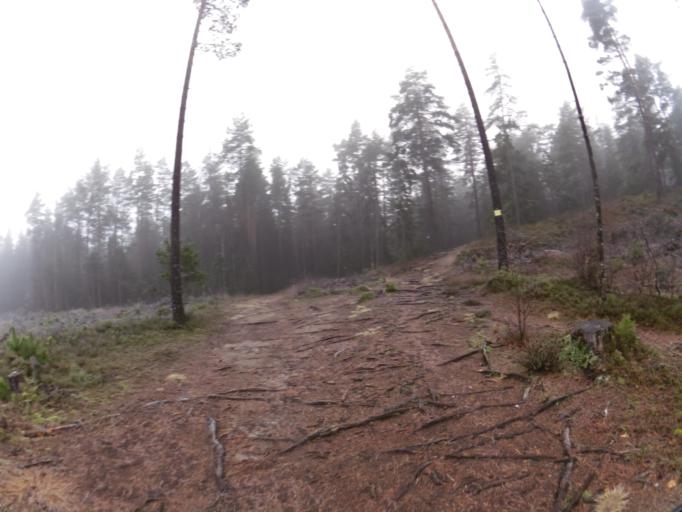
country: NO
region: Ostfold
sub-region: Fredrikstad
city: Fredrikstad
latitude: 59.2601
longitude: 10.9803
